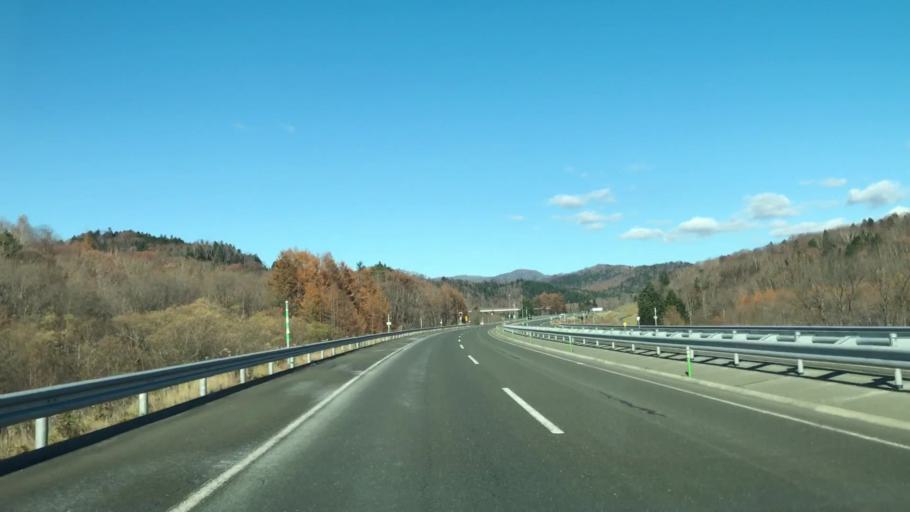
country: JP
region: Hokkaido
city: Shimo-furano
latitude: 42.9308
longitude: 142.2044
